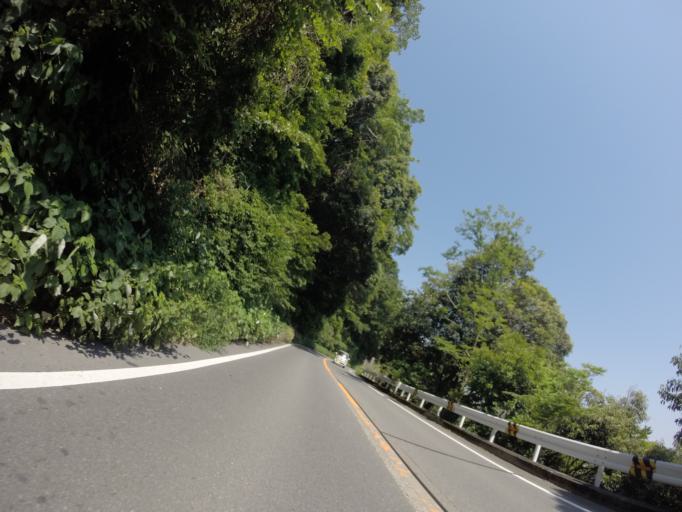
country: JP
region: Shizuoka
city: Fujinomiya
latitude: 35.1977
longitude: 138.5807
